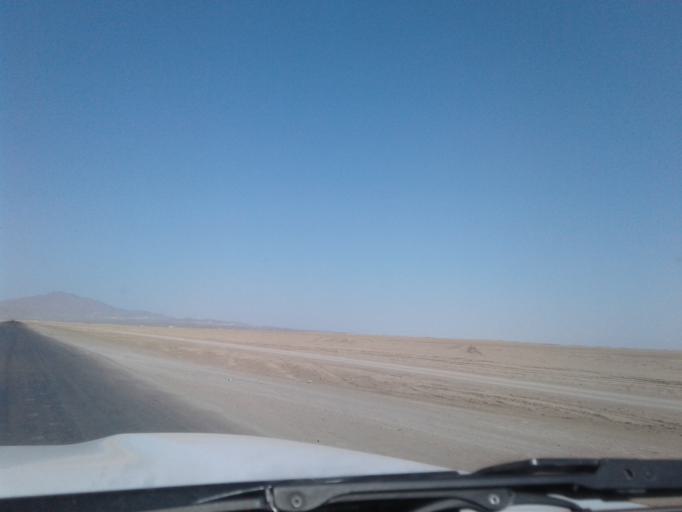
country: TM
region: Balkan
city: Gumdag
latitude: 39.2190
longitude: 54.6539
